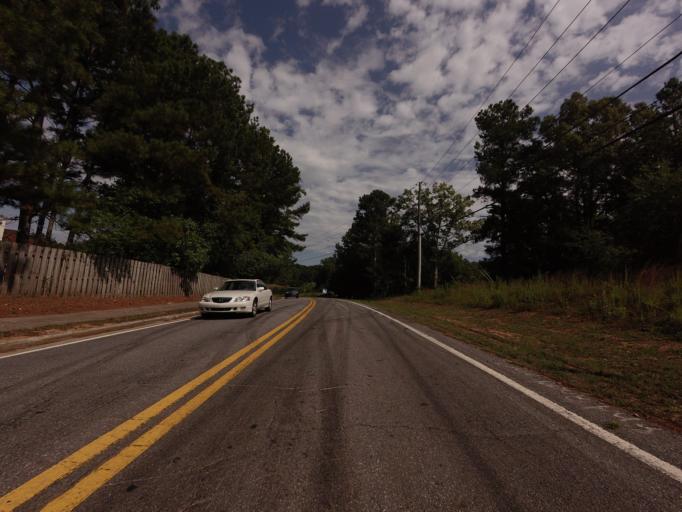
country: US
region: Georgia
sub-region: Gwinnett County
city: Duluth
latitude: 34.0409
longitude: -84.1572
